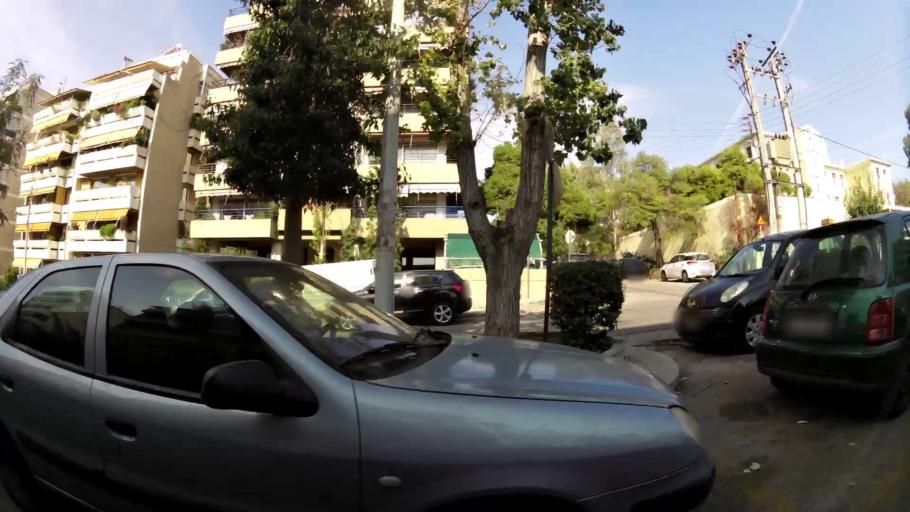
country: GR
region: Attica
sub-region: Nomarchia Athinas
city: Kallithea
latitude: 37.9465
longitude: 23.7054
